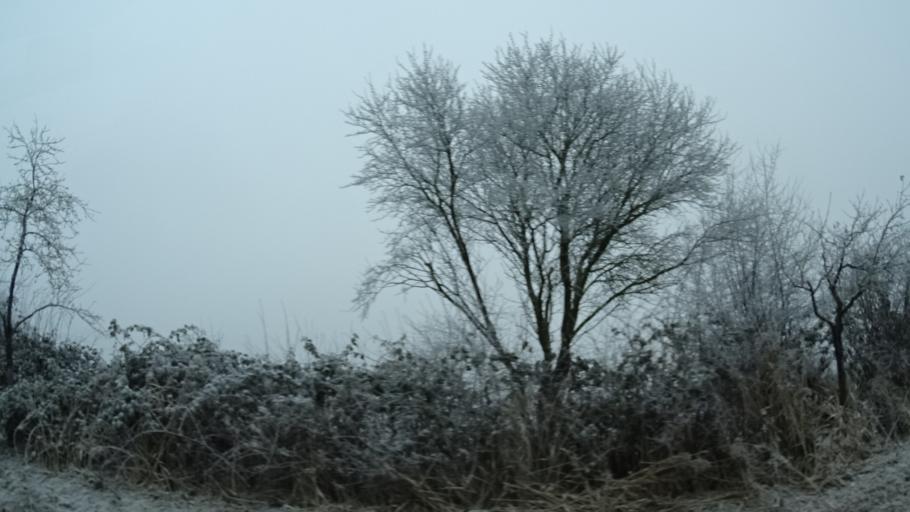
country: DE
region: Bavaria
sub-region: Regierungsbezirk Unterfranken
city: Volkach
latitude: 49.8324
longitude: 10.2525
